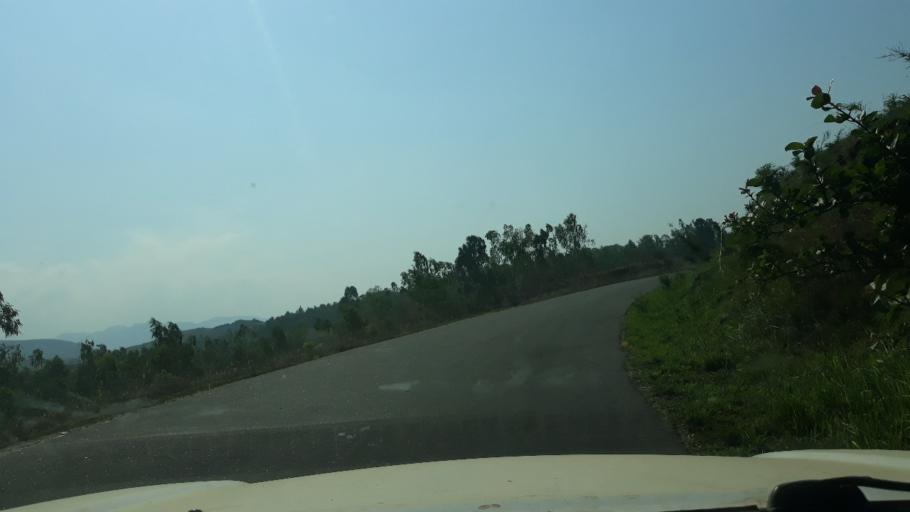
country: CD
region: South Kivu
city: Uvira
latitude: -3.2010
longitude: 29.1560
